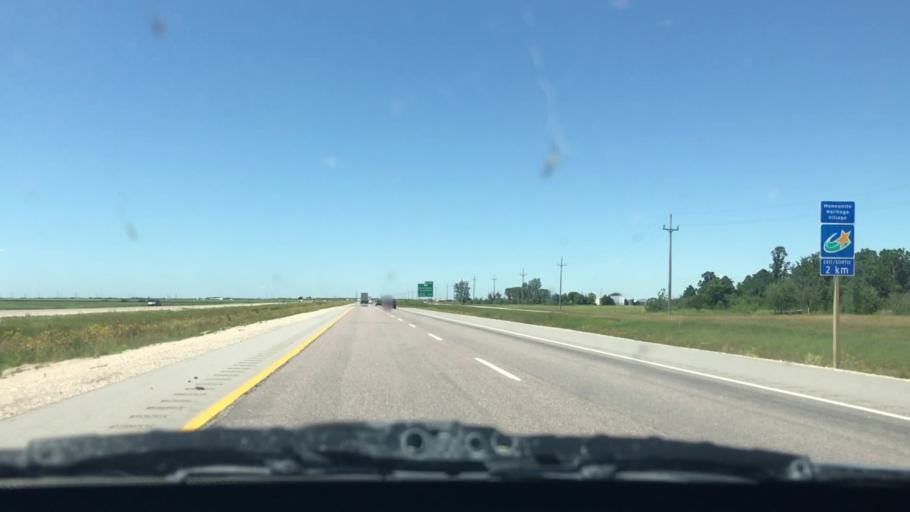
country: CA
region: Manitoba
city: Steinbach
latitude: 49.6874
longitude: -96.6114
